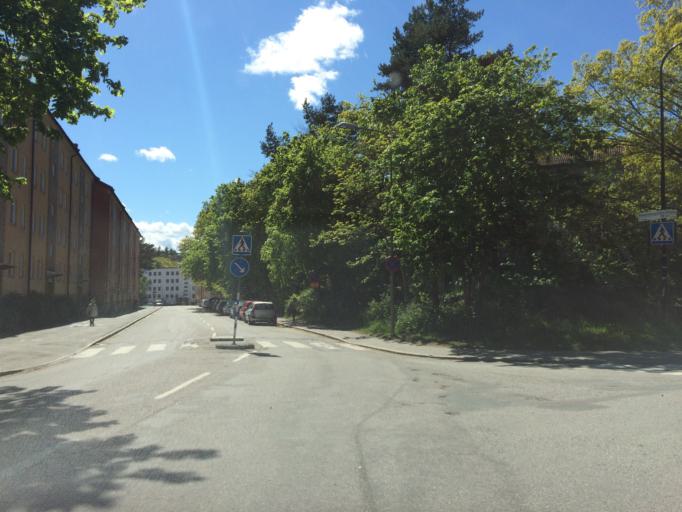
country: SE
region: Stockholm
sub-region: Solna Kommun
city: Solna
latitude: 59.3070
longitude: 17.9953
